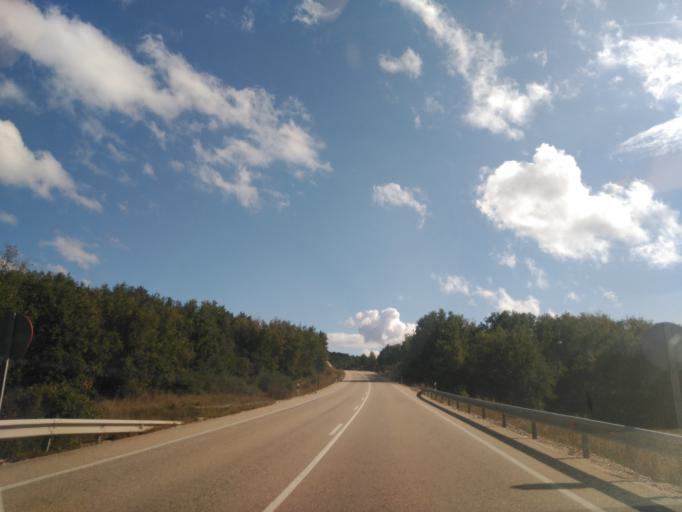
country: ES
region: Castille and Leon
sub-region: Provincia de Burgos
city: Pinilla de los Barruecos
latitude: 41.9193
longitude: -3.2795
